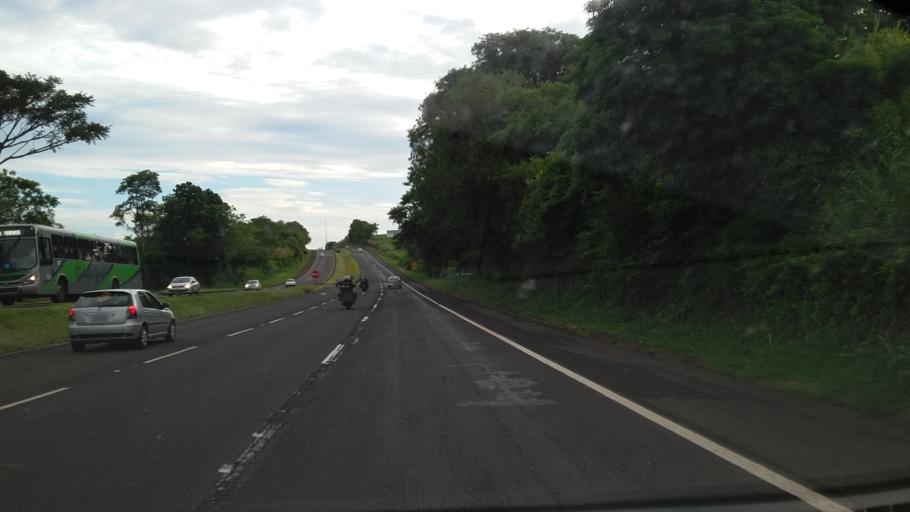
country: BR
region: Parana
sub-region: Paicandu
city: Paicandu
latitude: -23.5116
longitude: -52.0248
